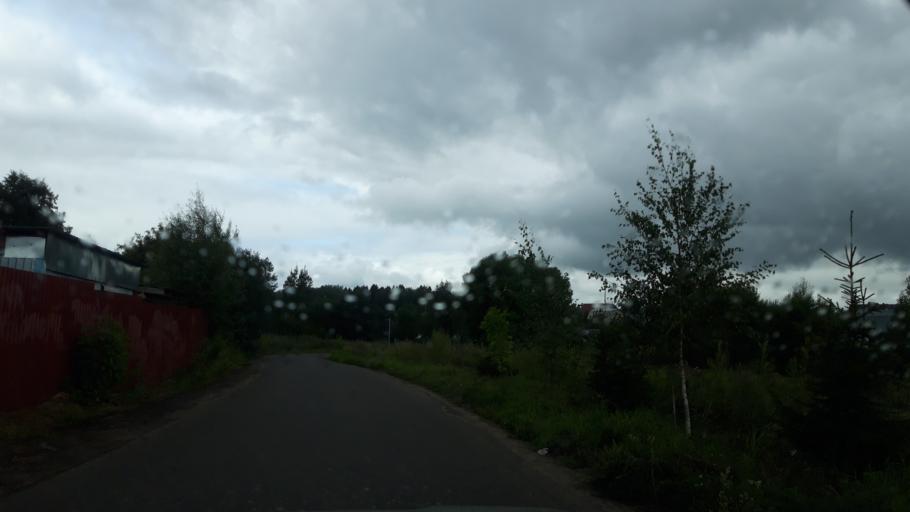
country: RU
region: Moskovskaya
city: Povarovo
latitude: 56.0967
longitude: 37.0690
